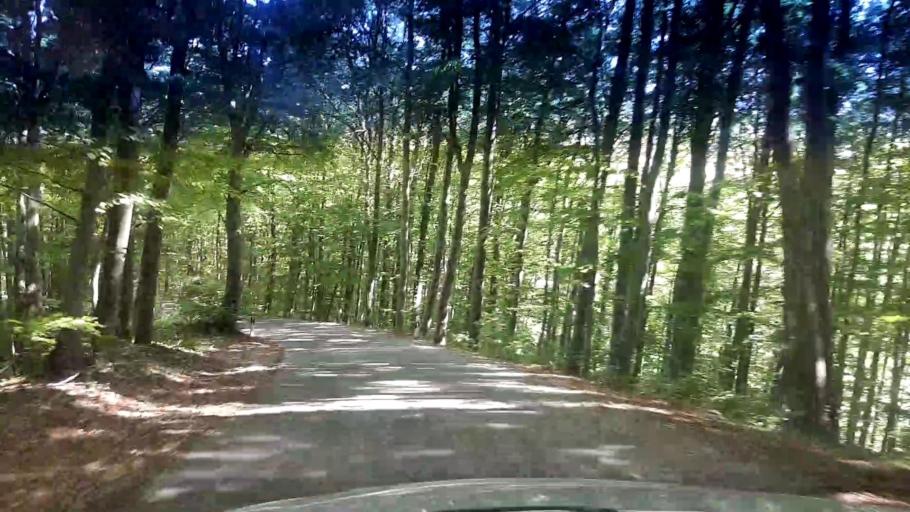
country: DE
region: Bavaria
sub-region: Upper Franconia
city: Schesslitz
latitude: 49.9515
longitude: 11.0628
